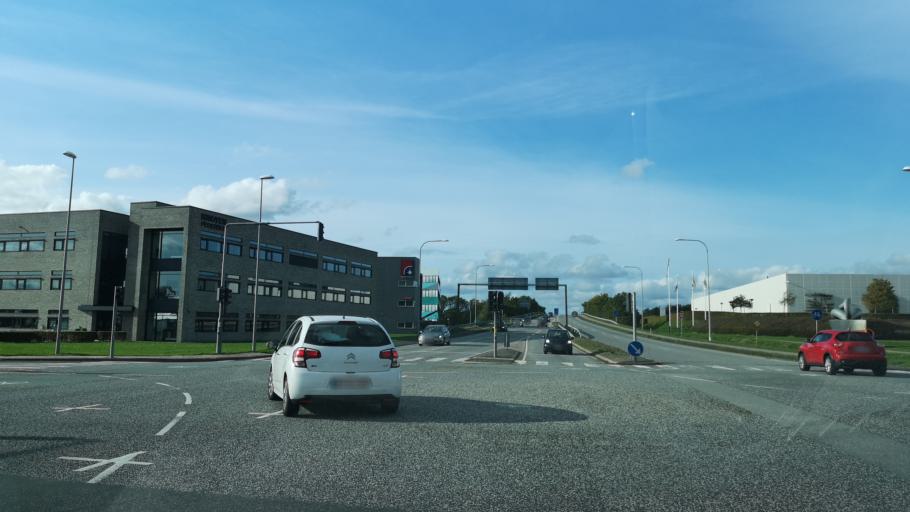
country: DK
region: Central Jutland
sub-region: Holstebro Kommune
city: Holstebro
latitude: 56.3724
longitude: 8.6272
